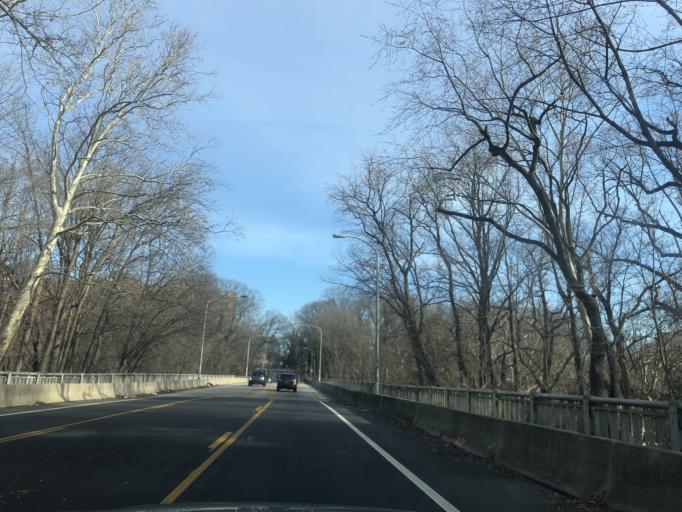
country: US
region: Pennsylvania
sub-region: Montgomery County
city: Wyndmoor
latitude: 40.0326
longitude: -75.1892
